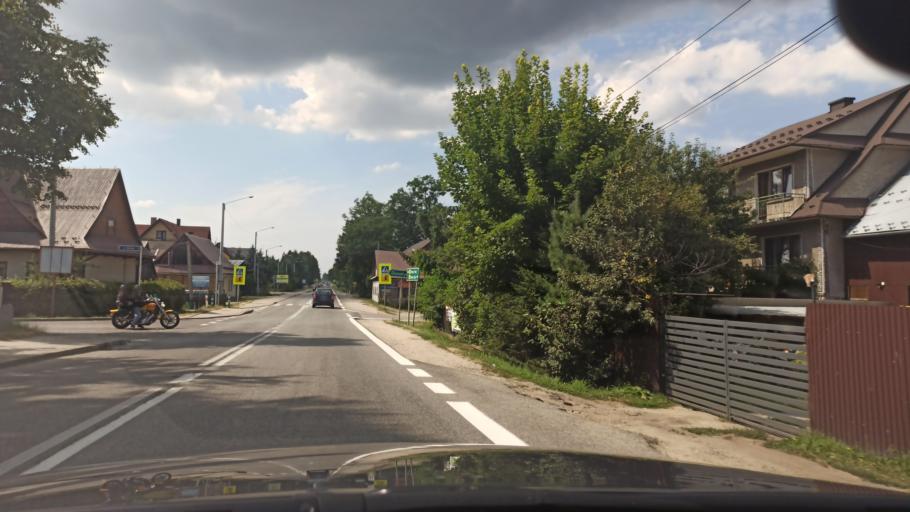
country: PL
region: Lesser Poland Voivodeship
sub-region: Powiat nowotarski
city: Lopuszna
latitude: 49.4705
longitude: 20.1324
